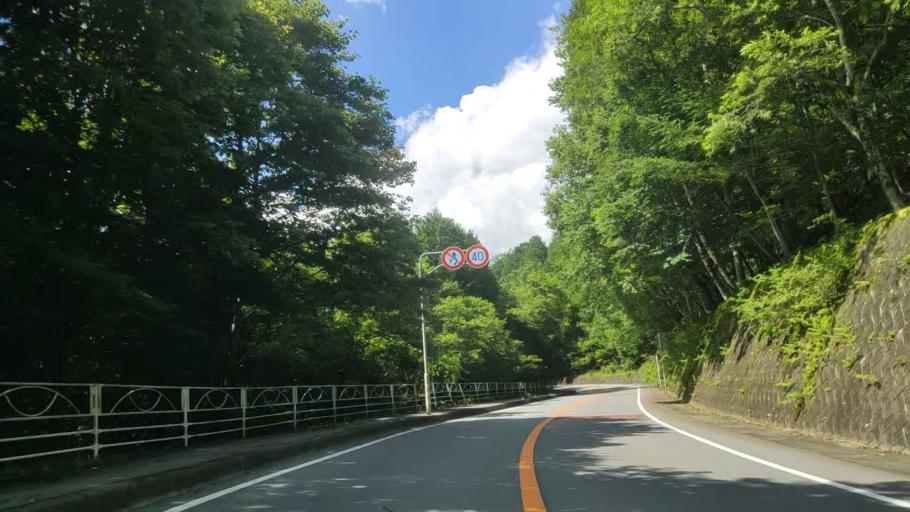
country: JP
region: Yamanashi
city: Enzan
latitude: 35.8548
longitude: 138.7575
